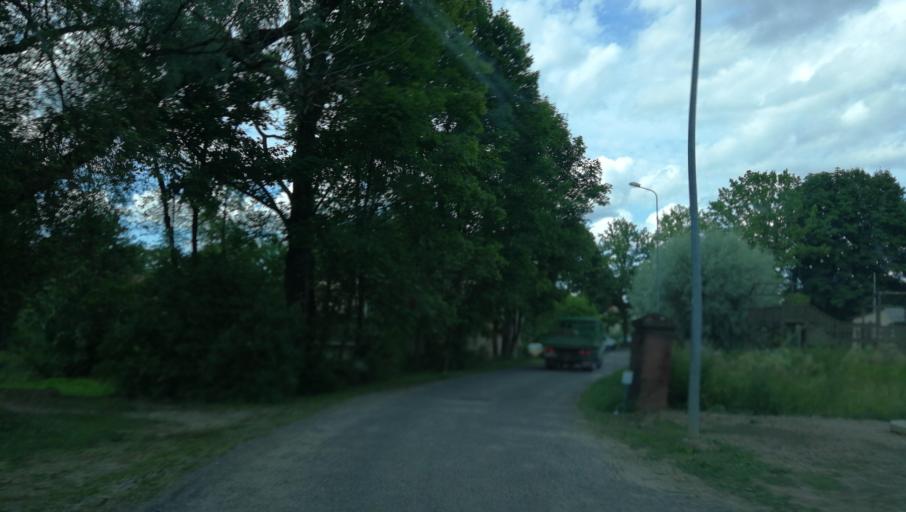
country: LV
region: Cesu Rajons
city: Cesis
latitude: 57.3070
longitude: 25.2712
